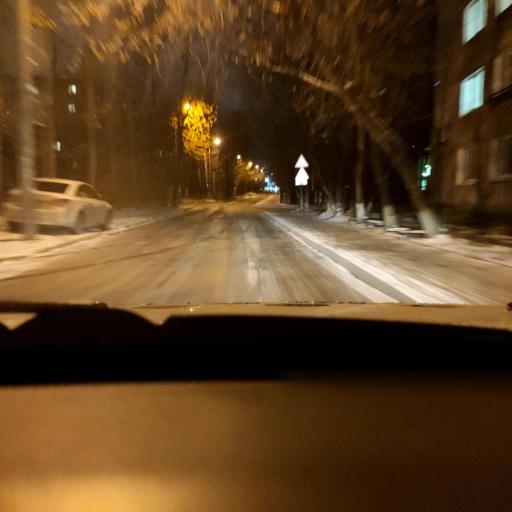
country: RU
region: Perm
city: Perm
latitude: 57.9974
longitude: 56.2131
